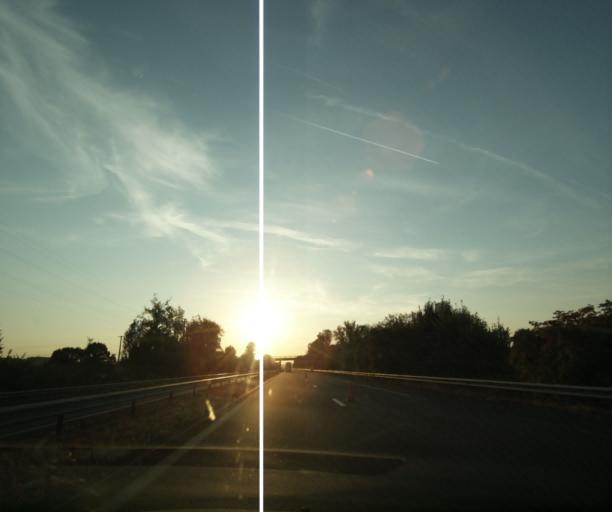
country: FR
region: Aquitaine
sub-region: Departement du Lot-et-Garonne
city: Sainte-Colombe-en-Bruilhois
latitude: 44.2119
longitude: 0.4584
